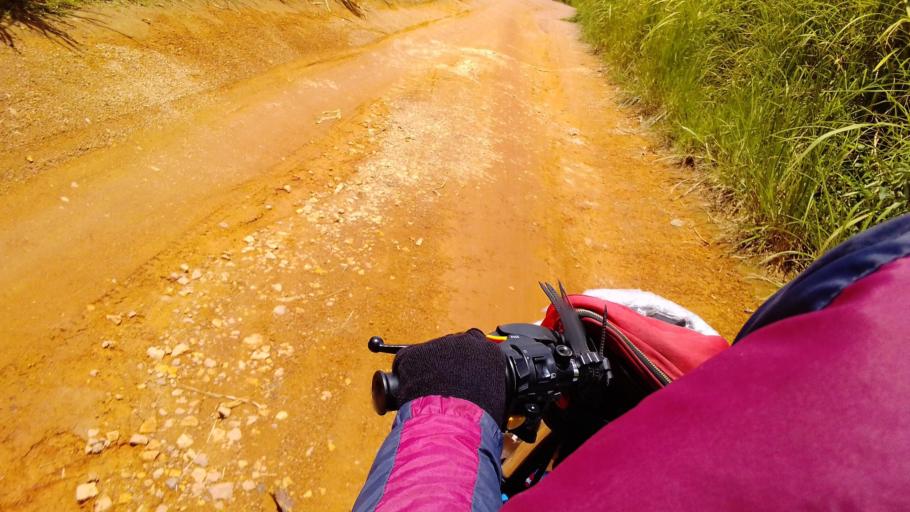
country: SL
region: Eastern Province
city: Koidu
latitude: 8.6864
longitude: -10.9561
